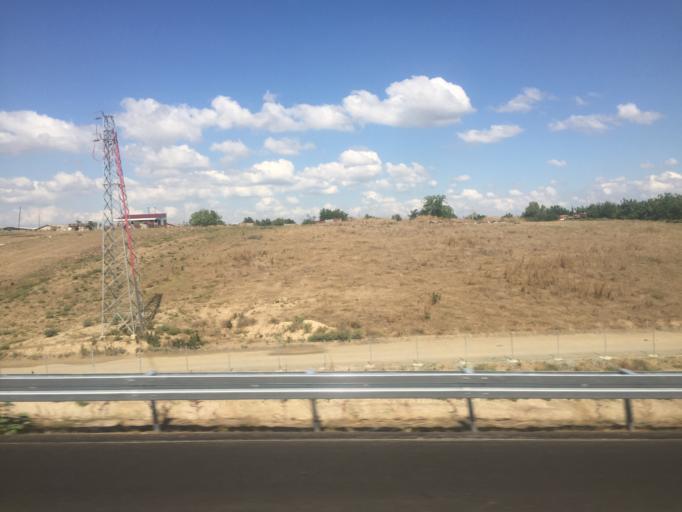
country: TR
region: Balikesir
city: Gobel
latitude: 40.0501
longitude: 28.2301
